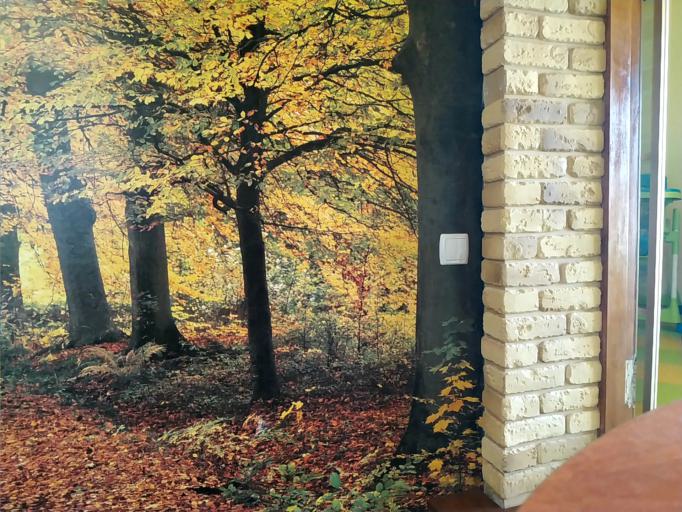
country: RU
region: Tverskaya
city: Rameshki
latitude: 57.4415
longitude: 36.0442
